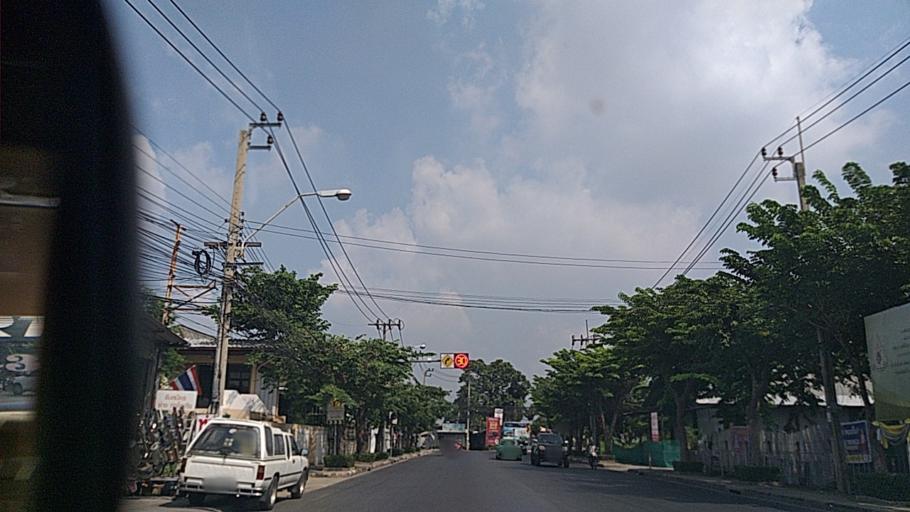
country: TH
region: Bangkok
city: Lat Phrao
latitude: 13.8232
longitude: 100.6088
